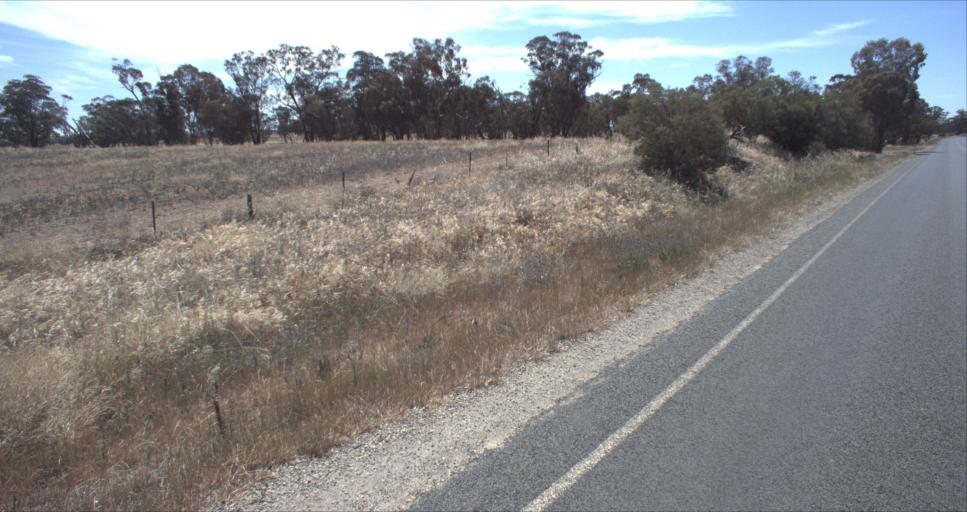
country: AU
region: New South Wales
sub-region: Leeton
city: Leeton
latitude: -34.6563
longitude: 146.4592
